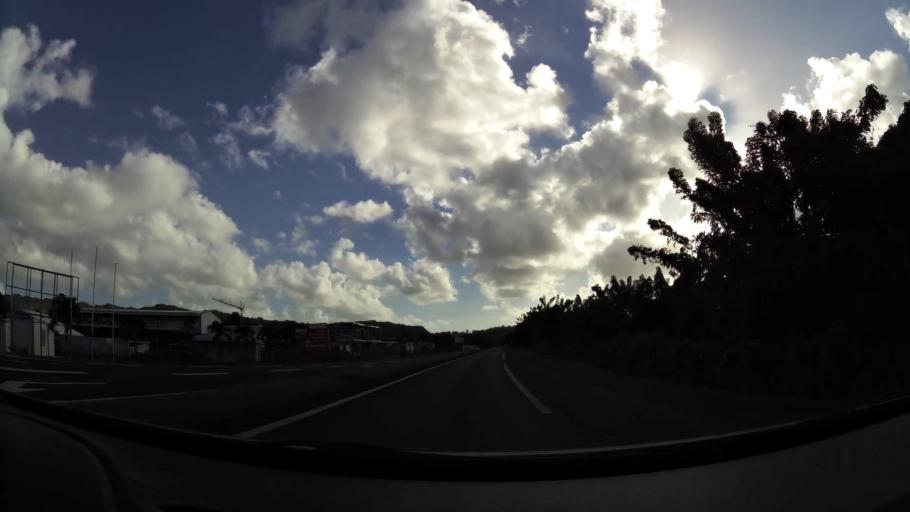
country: MQ
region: Martinique
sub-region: Martinique
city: Ducos
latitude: 14.6000
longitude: -60.9727
